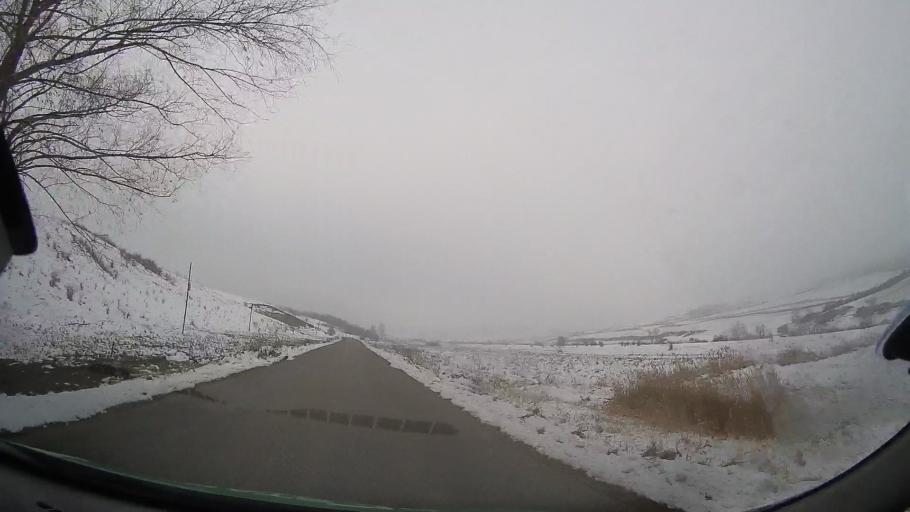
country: RO
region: Bacau
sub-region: Comuna Vultureni
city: Vultureni
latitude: 46.3171
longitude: 27.2929
